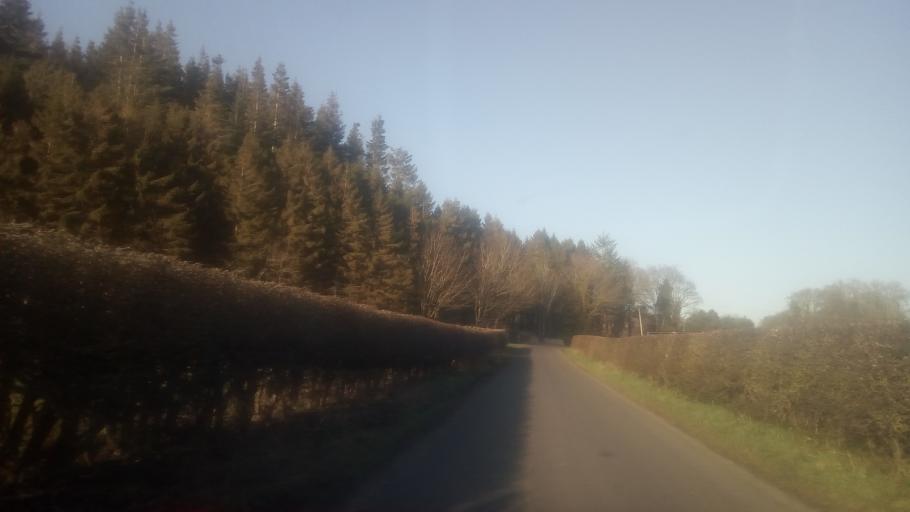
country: GB
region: Scotland
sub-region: The Scottish Borders
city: Saint Boswells
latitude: 55.4693
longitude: -2.6709
